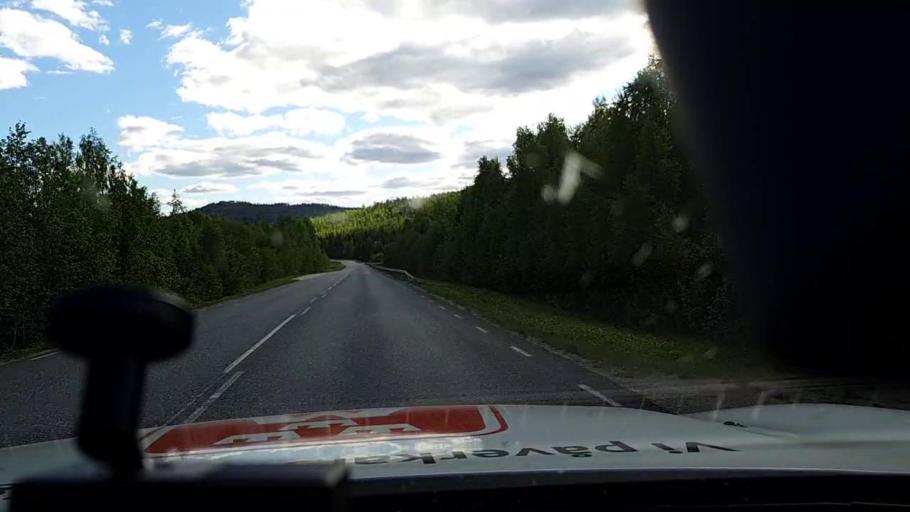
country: FI
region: Lapland
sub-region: Torniolaakso
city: Ylitornio
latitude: 66.3299
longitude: 23.6330
